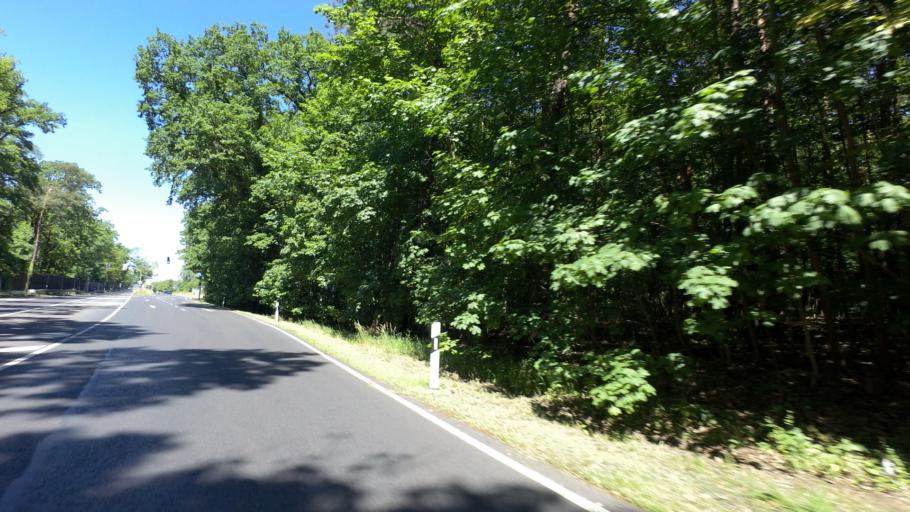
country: DE
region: Brandenburg
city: Rangsdorf
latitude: 52.2935
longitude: 13.4578
